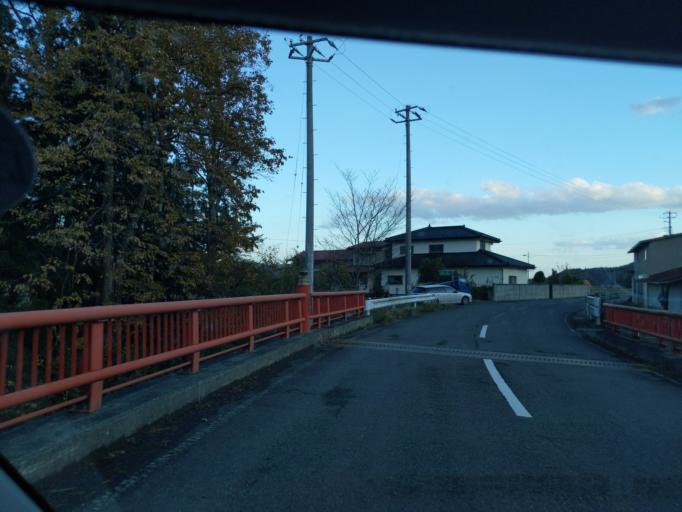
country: JP
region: Iwate
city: Mizusawa
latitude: 39.0427
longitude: 141.0501
